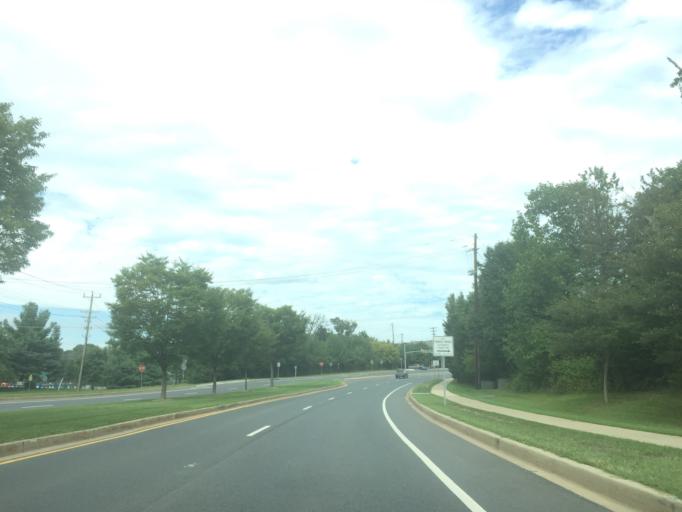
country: US
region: Maryland
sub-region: Montgomery County
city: North Potomac
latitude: 39.1256
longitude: -77.2458
